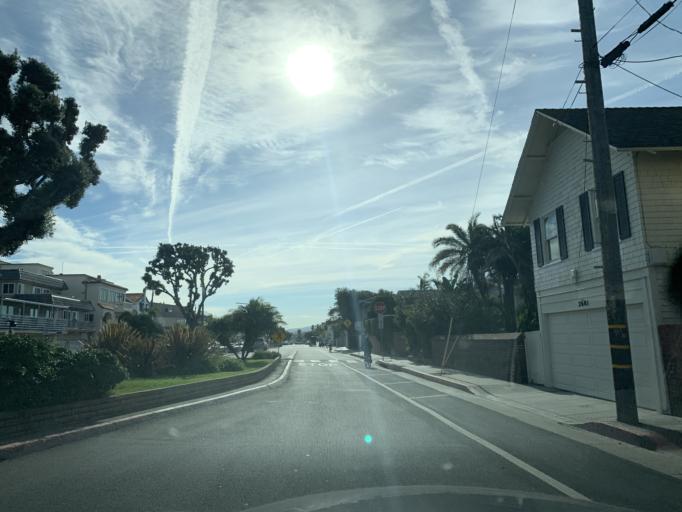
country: US
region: California
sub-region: Los Angeles County
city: Hermosa Beach
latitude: 33.8723
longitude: -118.4055
